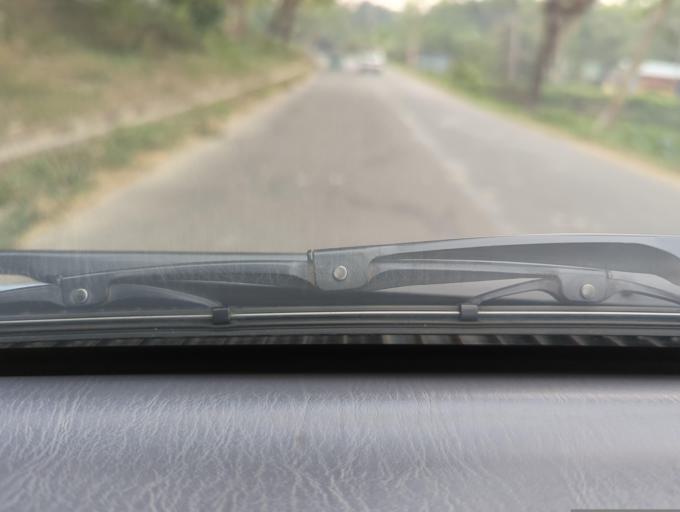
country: BD
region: Sylhet
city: Maulavi Bazar
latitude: 24.5131
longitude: 91.7258
